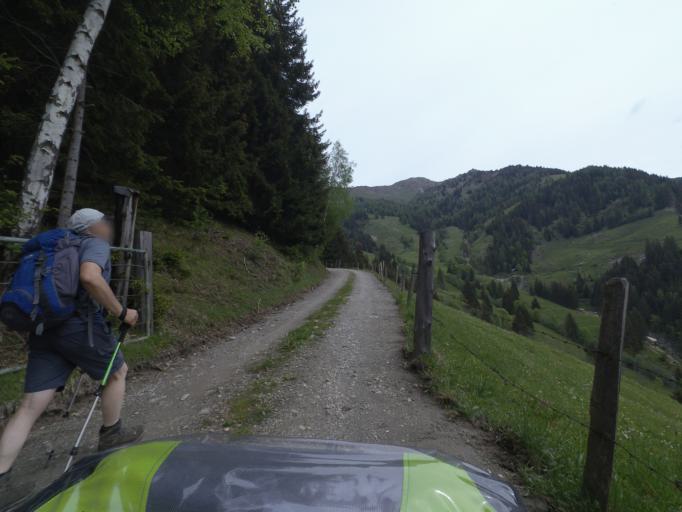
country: AT
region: Salzburg
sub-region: Politischer Bezirk Sankt Johann im Pongau
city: Dorfgastein
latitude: 47.2554
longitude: 13.1239
